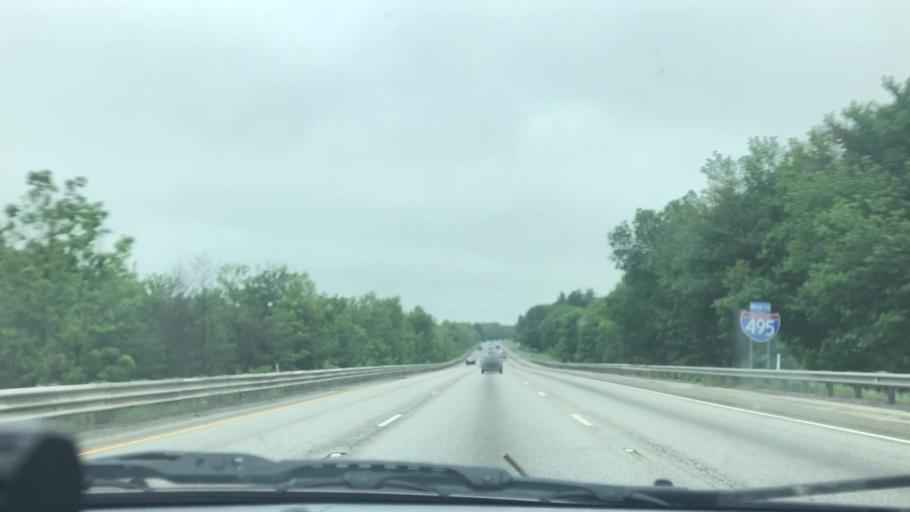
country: US
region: Massachusetts
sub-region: Worcester County
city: Berlin
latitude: 42.3972
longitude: -71.6069
